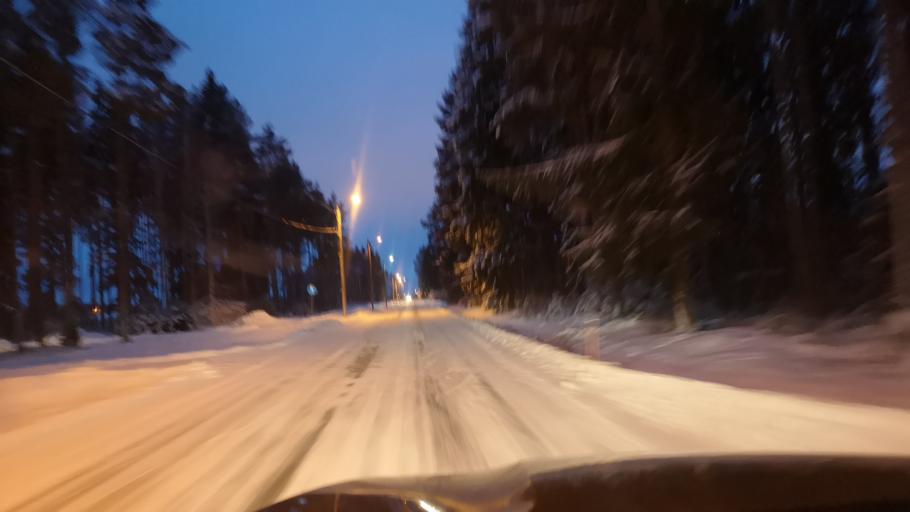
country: FI
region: Varsinais-Suomi
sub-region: Loimaa
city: Loimaa
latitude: 60.8678
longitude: 23.0869
